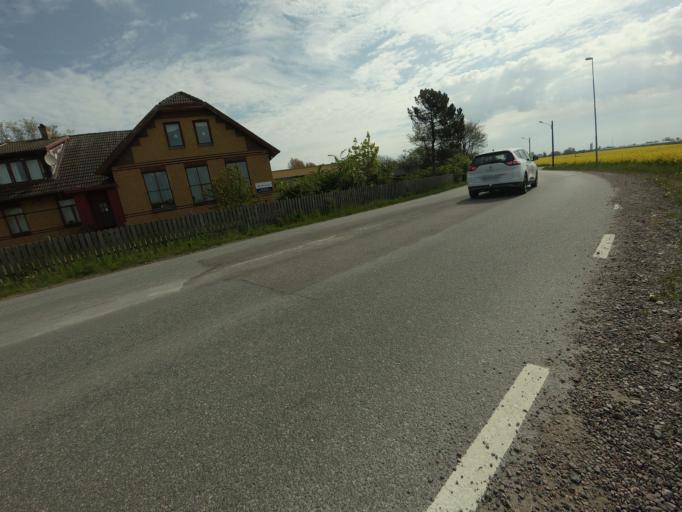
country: SE
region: Skane
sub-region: Hoganas Kommun
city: Hoganas
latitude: 56.2007
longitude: 12.5948
